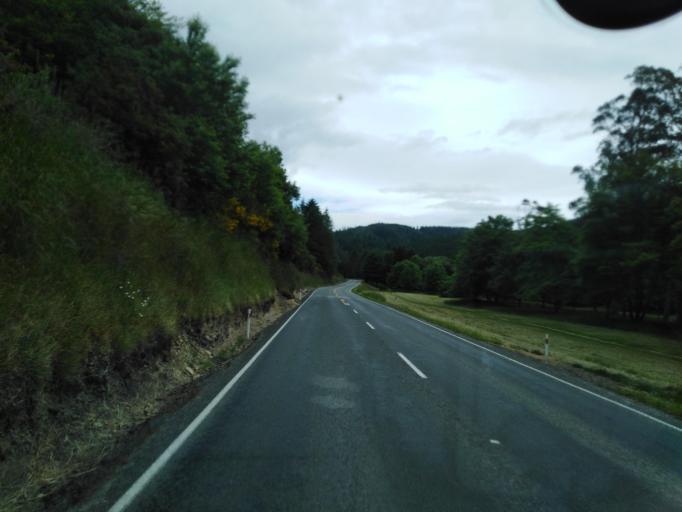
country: NZ
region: Tasman
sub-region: Tasman District
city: Wakefield
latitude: -41.4817
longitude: 172.8788
